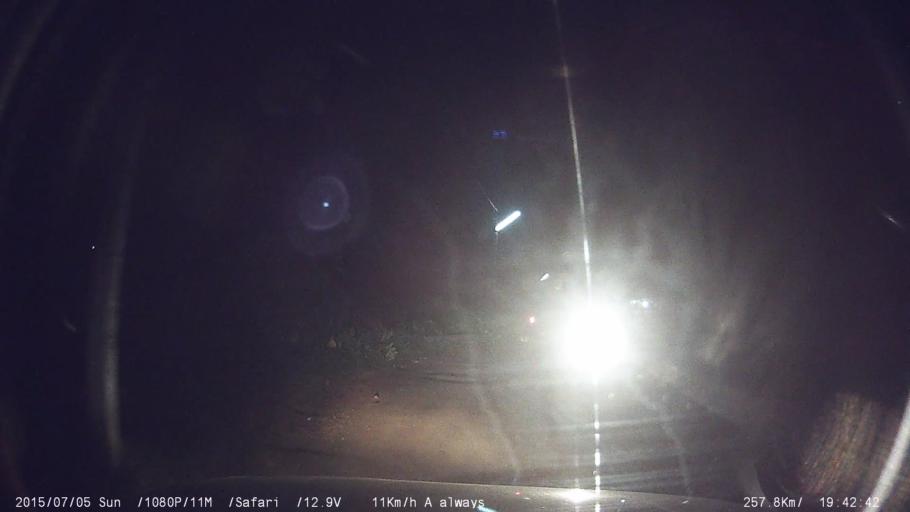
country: IN
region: Kerala
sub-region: Palakkad district
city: Palakkad
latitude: 10.7605
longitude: 76.5488
